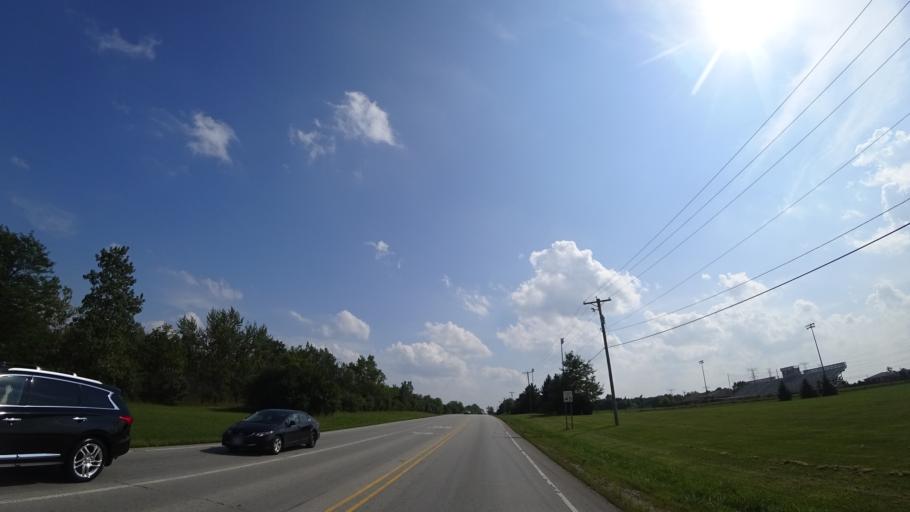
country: US
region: Illinois
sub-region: Will County
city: Goodings Grove
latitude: 41.6506
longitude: -87.9316
